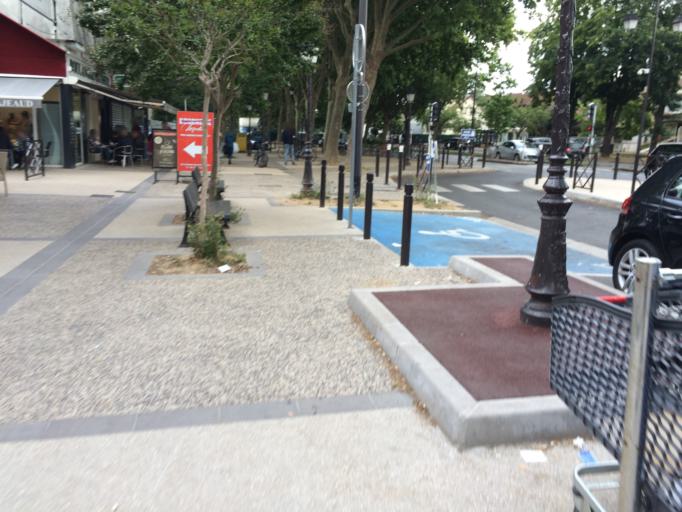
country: FR
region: Ile-de-France
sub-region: Departement de l'Essonne
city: Massy
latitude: 48.7412
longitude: 2.2825
